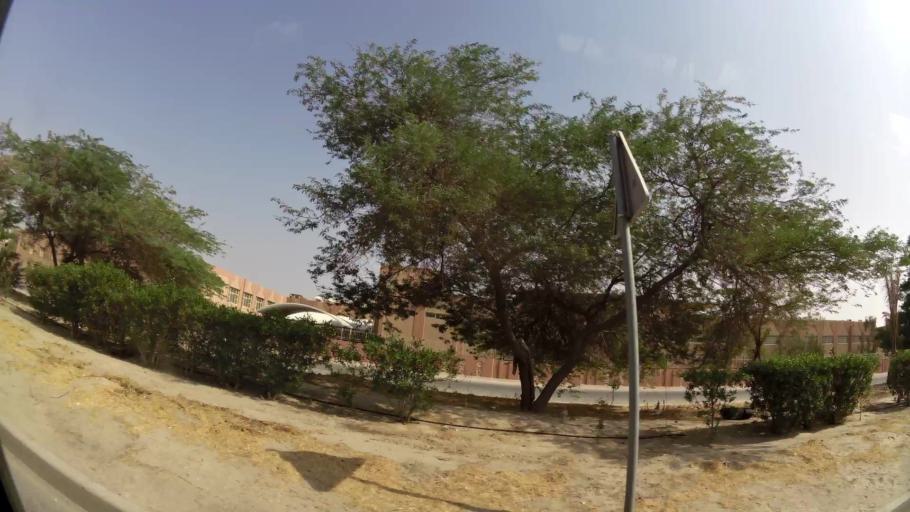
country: KW
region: Muhafazat al Jahra'
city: Al Jahra'
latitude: 29.3310
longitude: 47.6479
